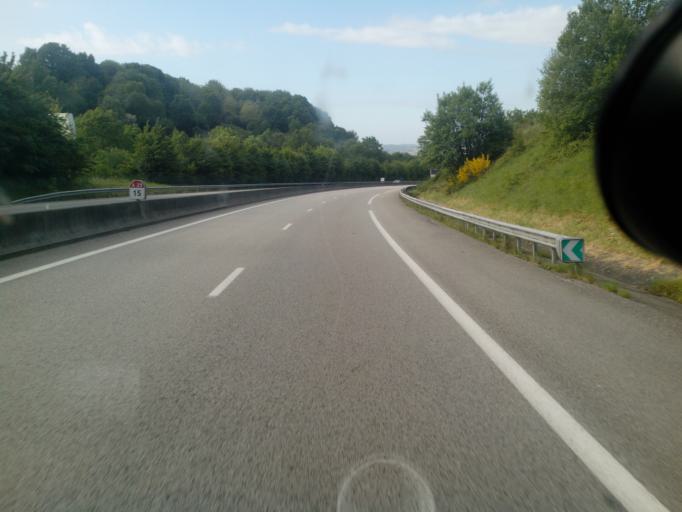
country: FR
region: Lower Normandy
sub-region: Departement du Calvados
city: La Riviere-Saint-Sauveur
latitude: 49.4002
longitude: 0.2613
